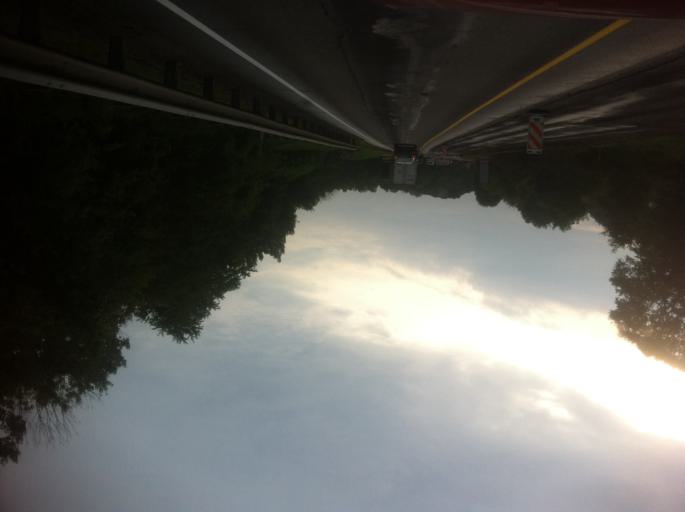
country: US
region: Pennsylvania
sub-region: Clarion County
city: Knox
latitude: 41.1933
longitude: -79.5683
